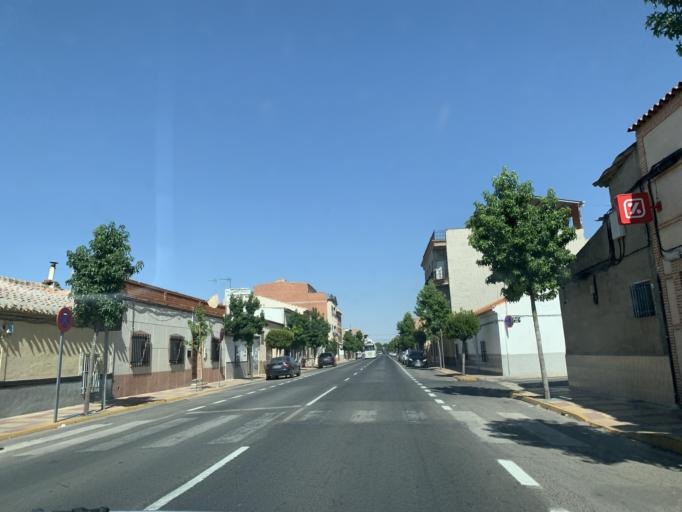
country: ES
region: Castille-La Mancha
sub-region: Provincia de Ciudad Real
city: Argamasilla de Alba
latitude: 39.1286
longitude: -3.1002
